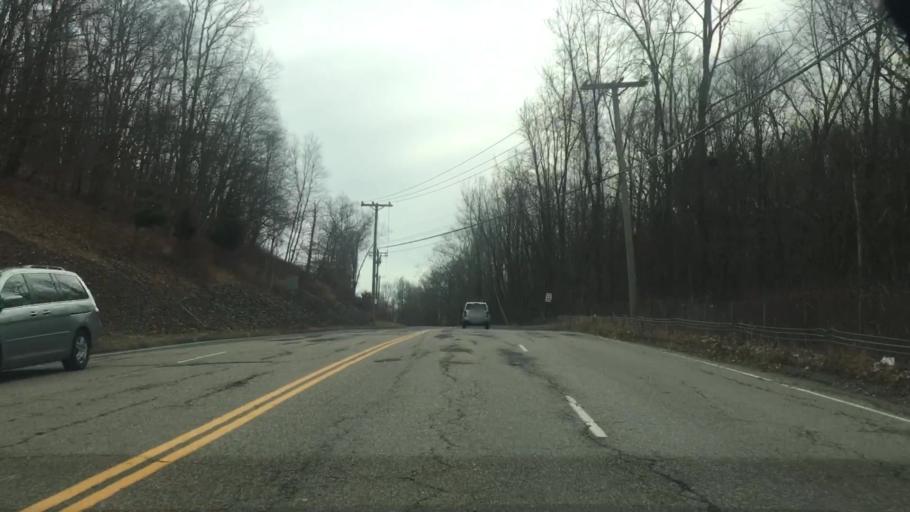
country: US
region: New York
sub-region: Putnam County
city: Peach Lake
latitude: 41.3884
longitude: -73.5401
